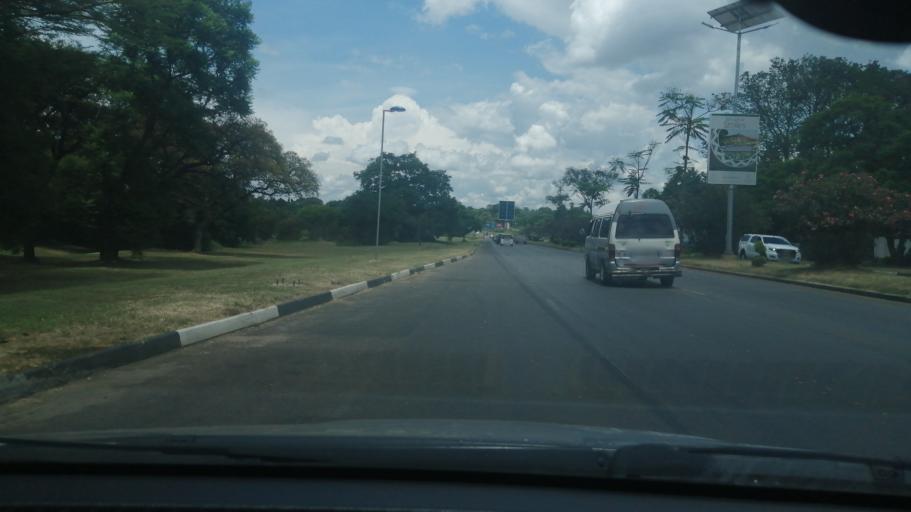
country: ZW
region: Harare
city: Harare
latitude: -17.8319
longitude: 31.1016
